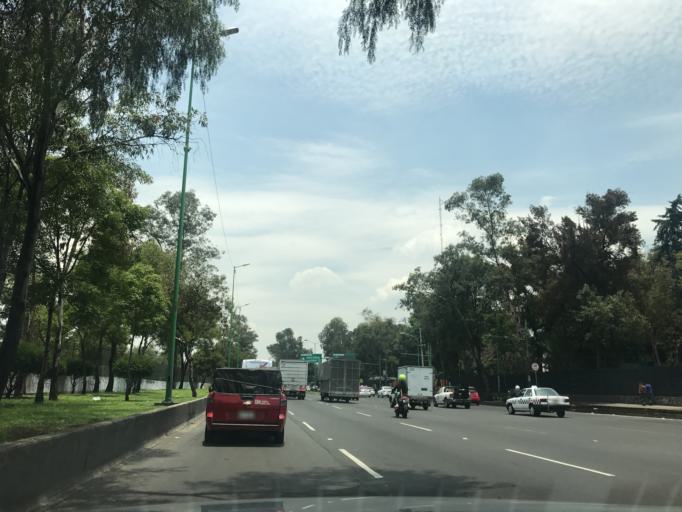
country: MX
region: Mexico
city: Colonia Lindavista
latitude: 19.4830
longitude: -99.1420
